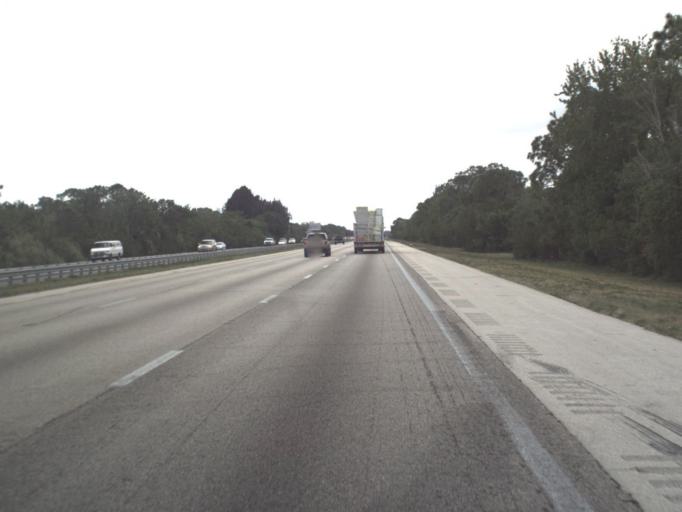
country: US
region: Florida
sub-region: Brevard County
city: South Patrick Shores
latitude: 28.1741
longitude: -80.7060
